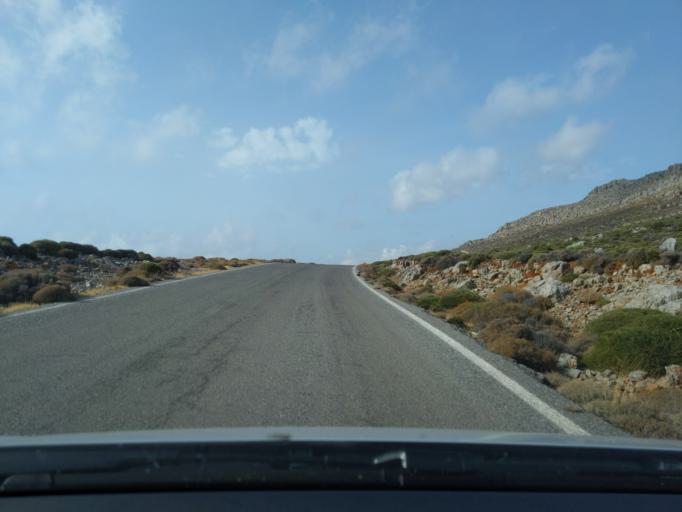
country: GR
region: Crete
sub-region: Nomos Lasithiou
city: Palekastro
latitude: 35.0871
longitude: 26.2663
